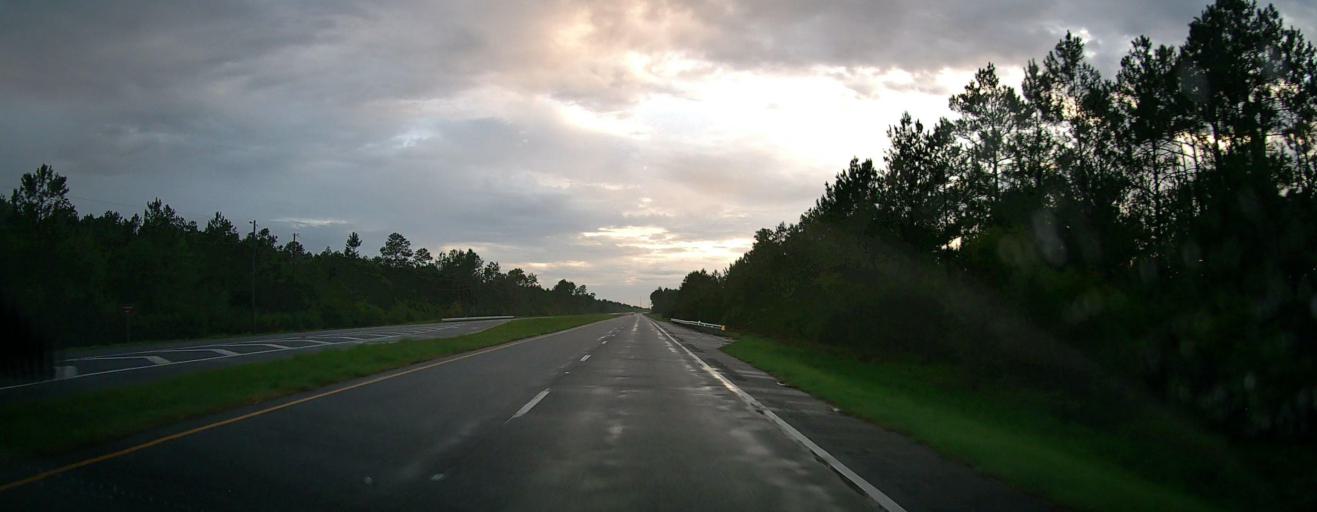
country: US
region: Georgia
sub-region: Clinch County
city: Homerville
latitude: 30.9763
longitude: -82.9043
